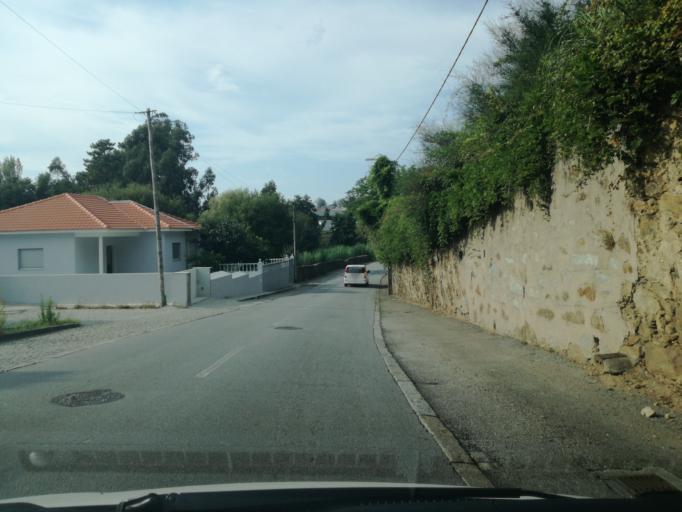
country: PT
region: Porto
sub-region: Vila Nova de Gaia
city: Arcozelo
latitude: 41.0590
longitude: -8.6275
